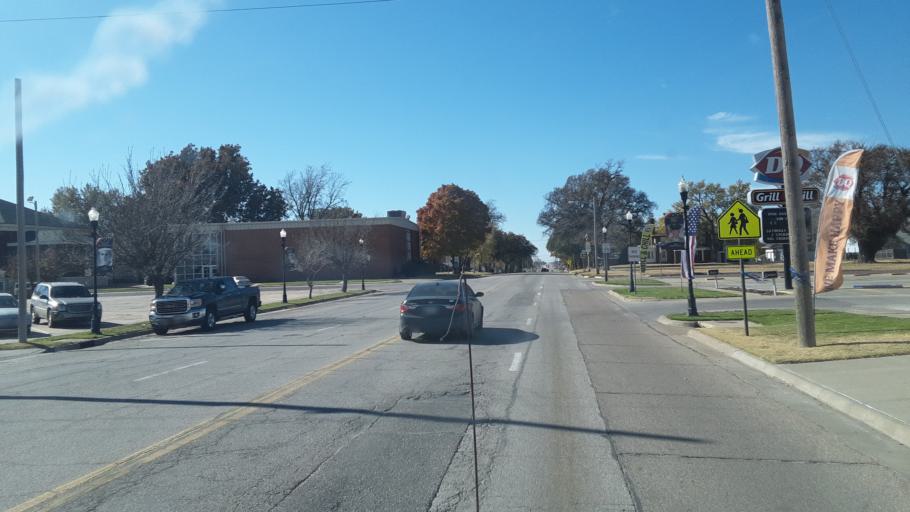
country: US
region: Kansas
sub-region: Rice County
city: Lyons
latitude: 38.3478
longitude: -98.2051
